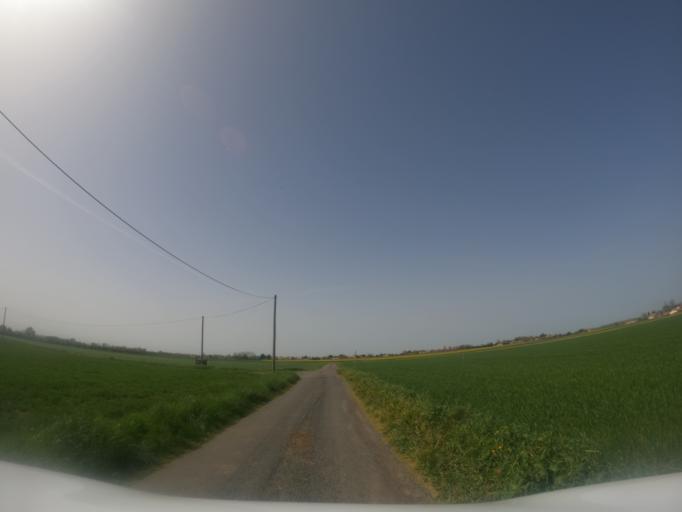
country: FR
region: Pays de la Loire
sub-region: Departement de la Vendee
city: Maillezais
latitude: 46.3867
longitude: -0.7954
